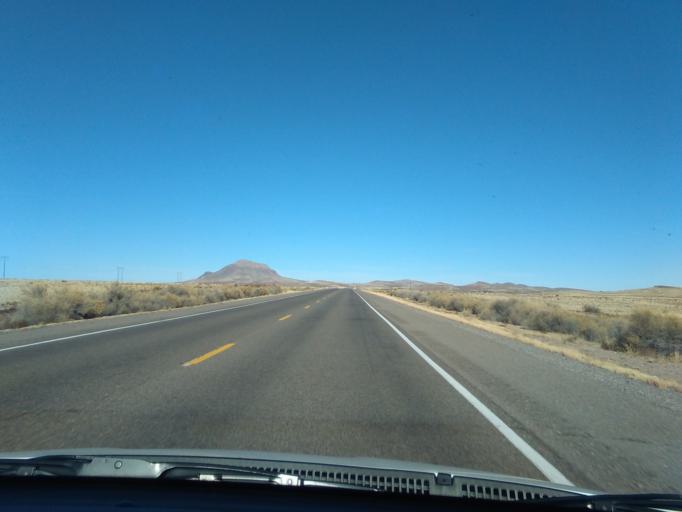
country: US
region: New Mexico
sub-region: Dona Ana County
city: Hatch
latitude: 32.5502
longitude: -107.4772
